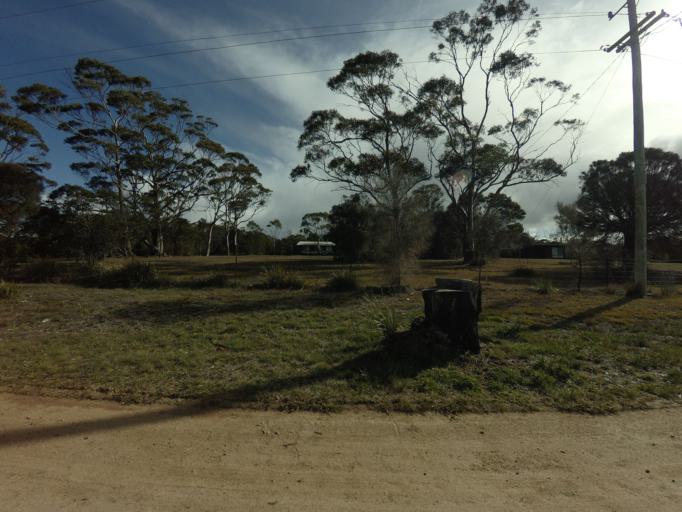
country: AU
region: Tasmania
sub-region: Sorell
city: Sorell
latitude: -42.3053
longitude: 147.9965
